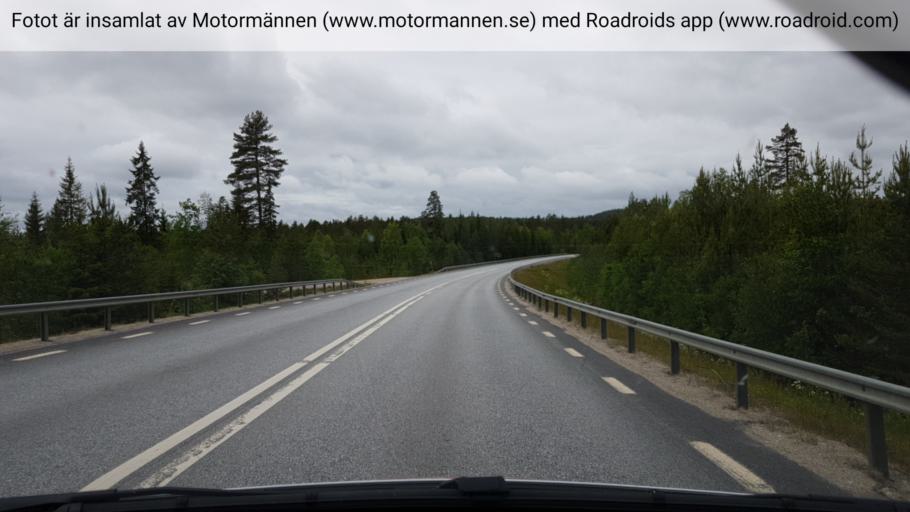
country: SE
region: Vaesterbotten
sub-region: Vannas Kommun
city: Vaennaes
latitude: 64.0115
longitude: 19.6978
